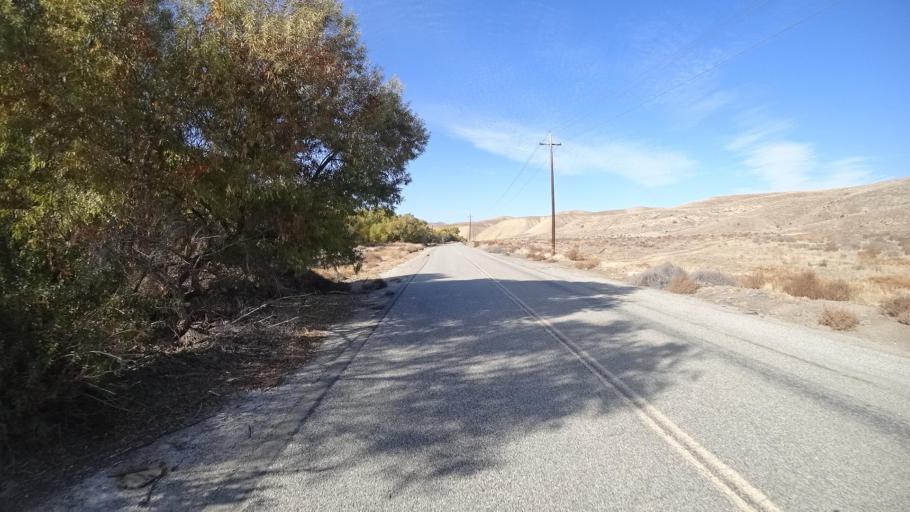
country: US
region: California
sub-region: Kern County
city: Oildale
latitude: 35.5259
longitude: -118.9491
